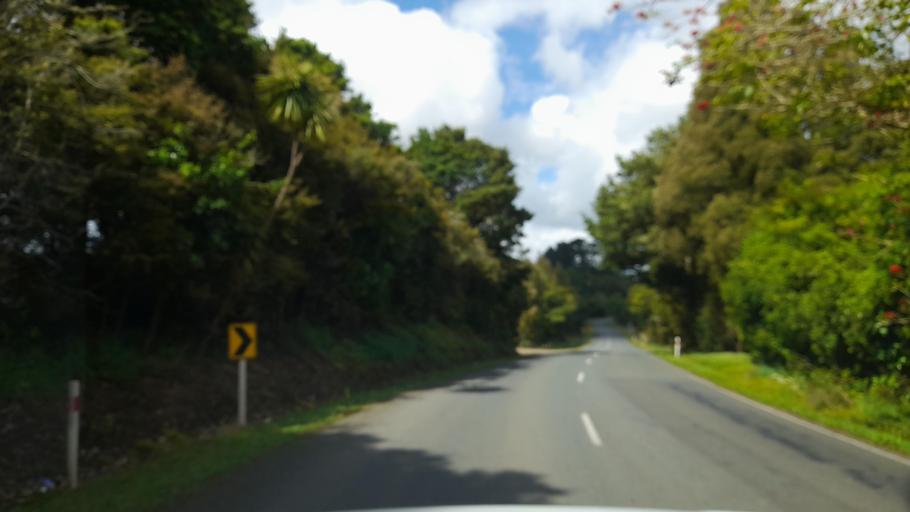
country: NZ
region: Northland
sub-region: Whangarei
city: Maungatapere
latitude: -35.6512
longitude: 174.1419
